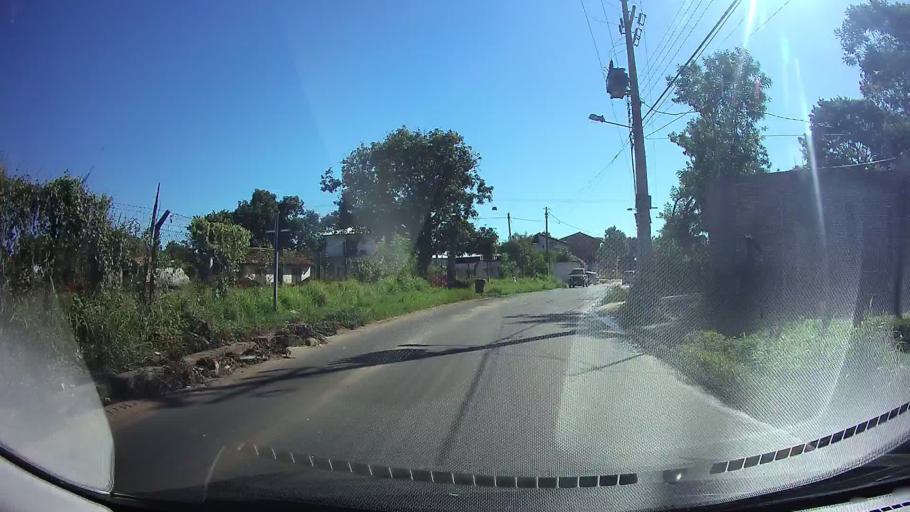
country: PY
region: Central
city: Fernando de la Mora
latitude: -25.2969
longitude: -57.5304
